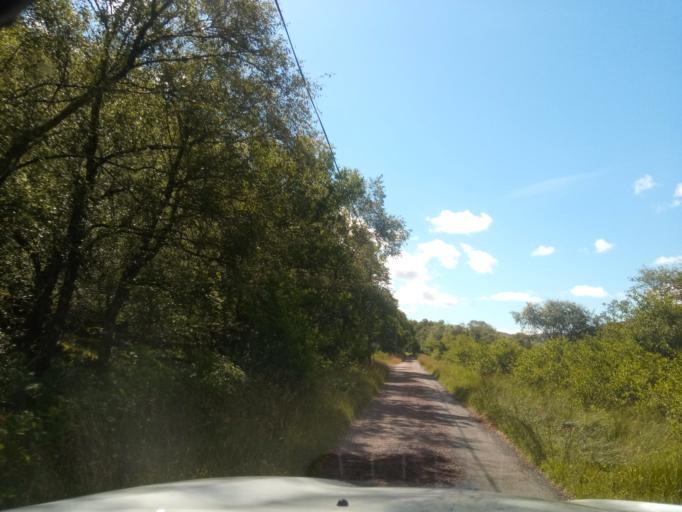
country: GB
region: Scotland
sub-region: Argyll and Bute
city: Isle Of Mull
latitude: 56.7674
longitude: -5.8222
